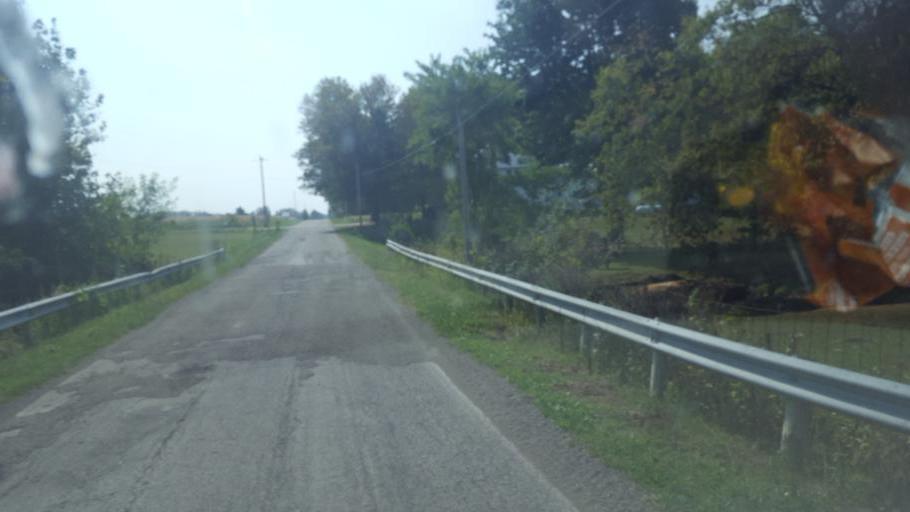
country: US
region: Ohio
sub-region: Morrow County
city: Mount Gilead
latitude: 40.5899
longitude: -82.8427
